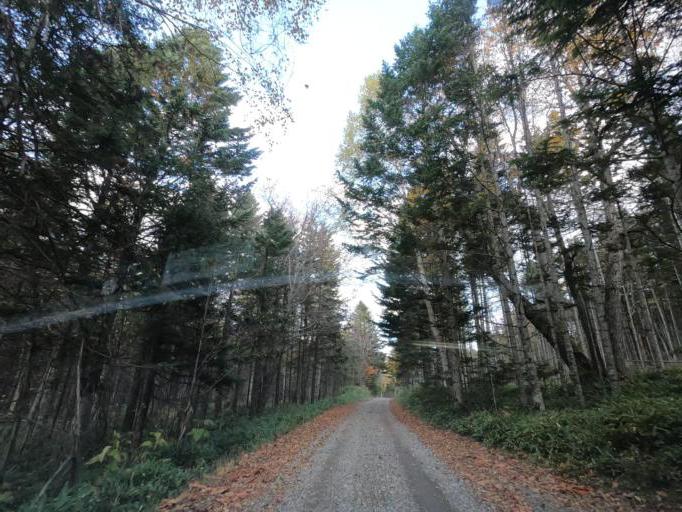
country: JP
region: Hokkaido
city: Otofuke
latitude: 43.4333
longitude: 143.1511
